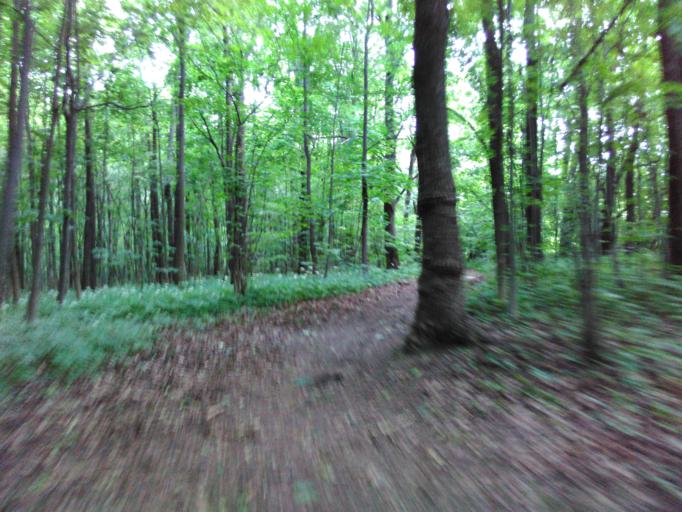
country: RU
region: Moscow
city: Yasenevo
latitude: 55.6320
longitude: 37.5428
